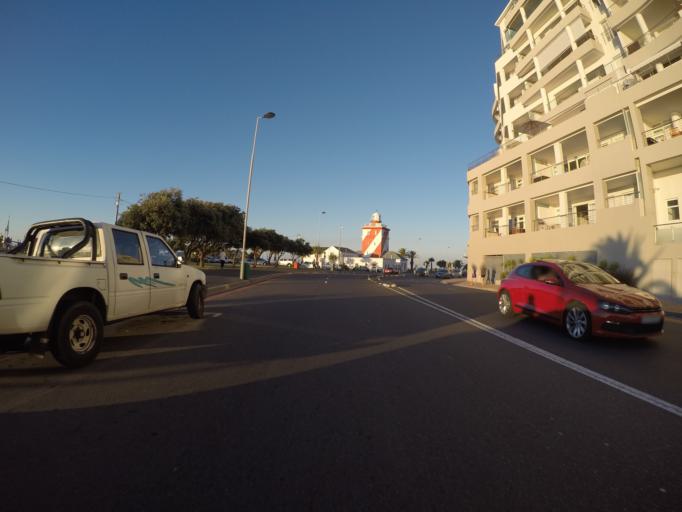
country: ZA
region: Western Cape
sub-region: City of Cape Town
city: Cape Town
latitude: -33.9025
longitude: 18.3992
